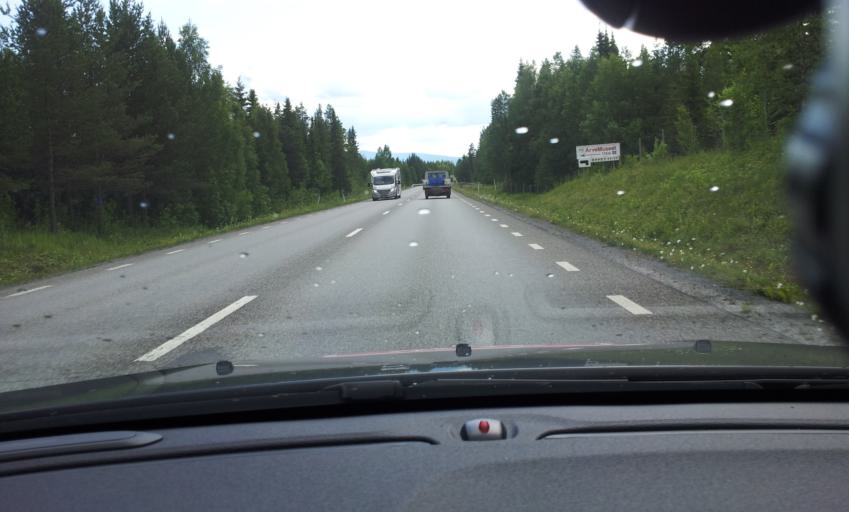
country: SE
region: Jaemtland
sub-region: Krokoms Kommun
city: Valla
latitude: 63.3155
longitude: 13.9323
